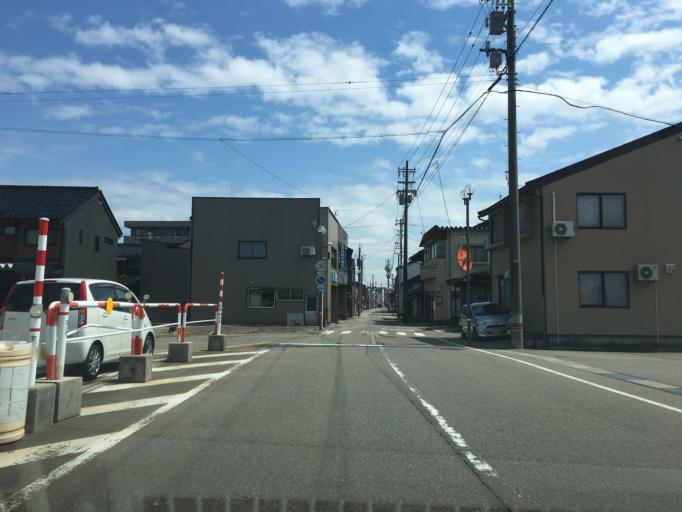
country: JP
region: Toyama
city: Nishishinminato
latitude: 36.7973
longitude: 137.0582
